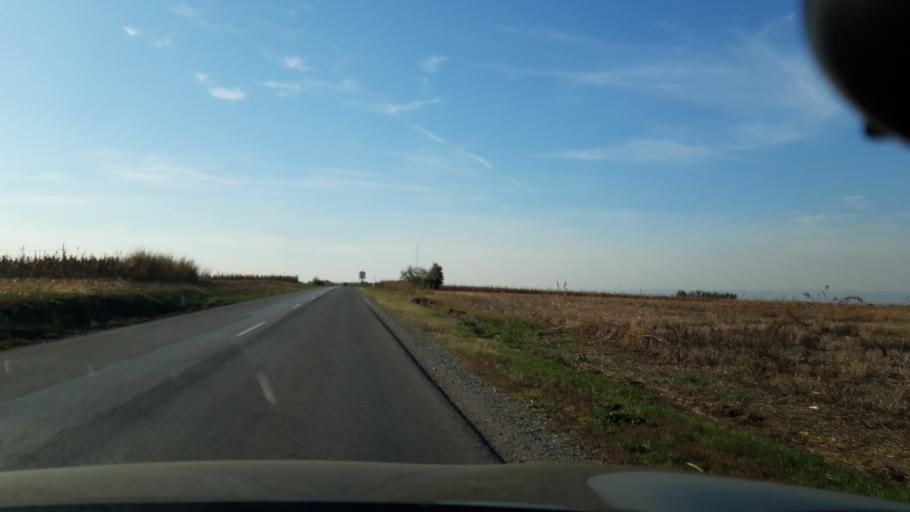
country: RS
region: Autonomna Pokrajina Vojvodina
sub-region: Sremski Okrug
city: Ruma
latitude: 45.0090
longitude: 19.8917
